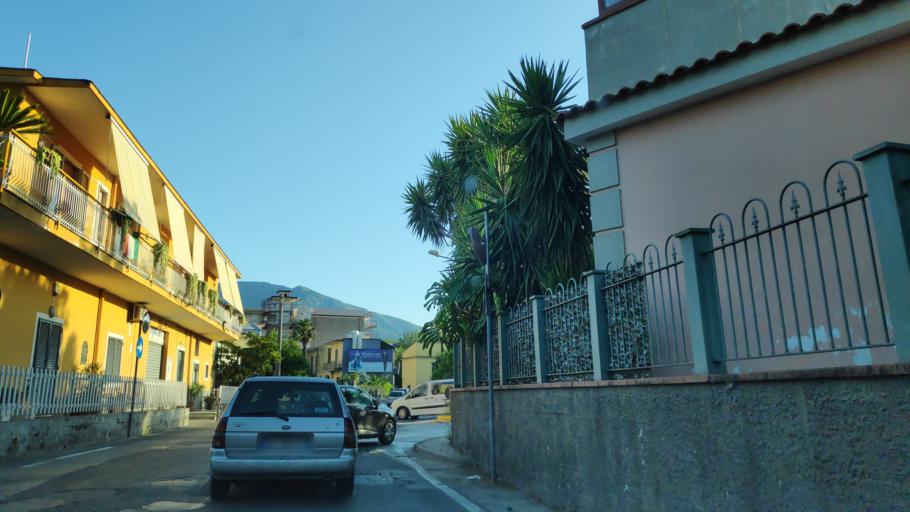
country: IT
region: Campania
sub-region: Provincia di Salerno
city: Pagani
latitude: 40.7538
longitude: 14.6158
